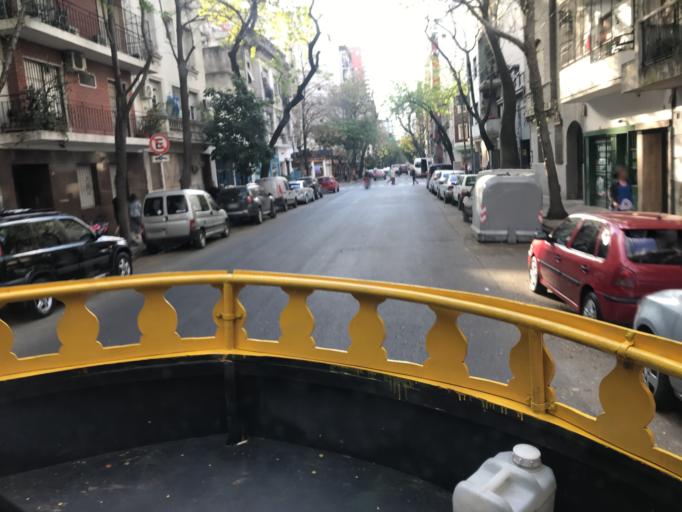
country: AR
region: Buenos Aires F.D.
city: Retiro
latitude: -34.5881
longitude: -58.4173
